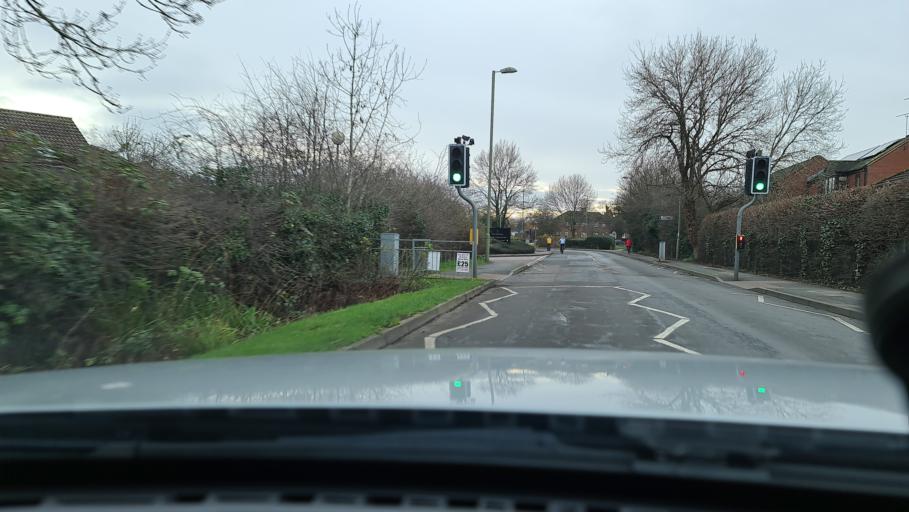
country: GB
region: England
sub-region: Oxfordshire
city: Banbury
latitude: 52.0677
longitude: -1.3210
